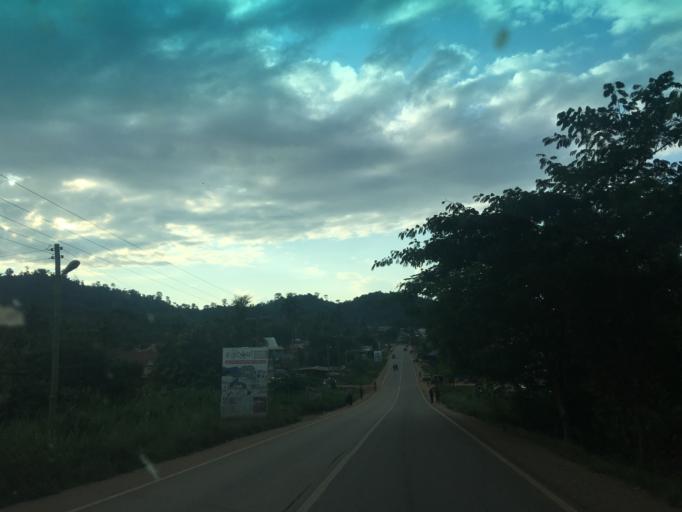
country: GH
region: Western
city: Bibiani
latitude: 6.4598
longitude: -2.3205
